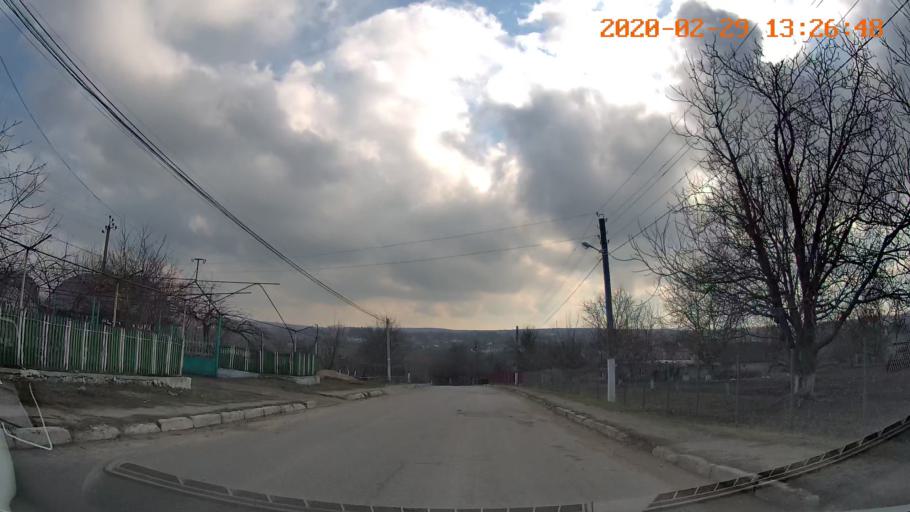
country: MD
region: Telenesti
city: Camenca
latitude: 47.9170
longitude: 28.6391
